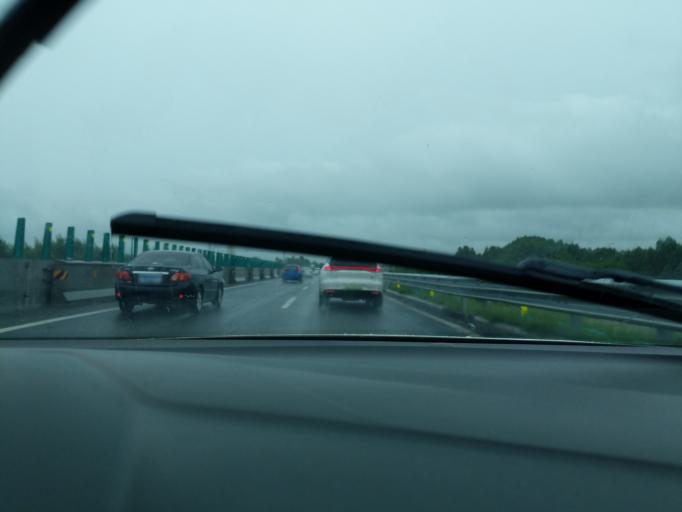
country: CN
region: Guangdong
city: Yueshan
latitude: 22.4616
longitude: 112.6916
